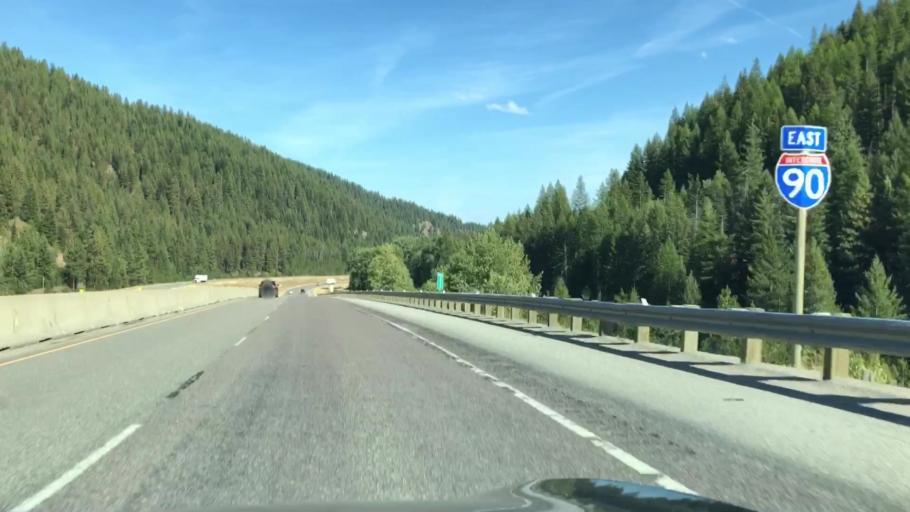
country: US
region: Montana
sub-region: Sanders County
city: Thompson Falls
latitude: 47.4075
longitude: -115.5021
